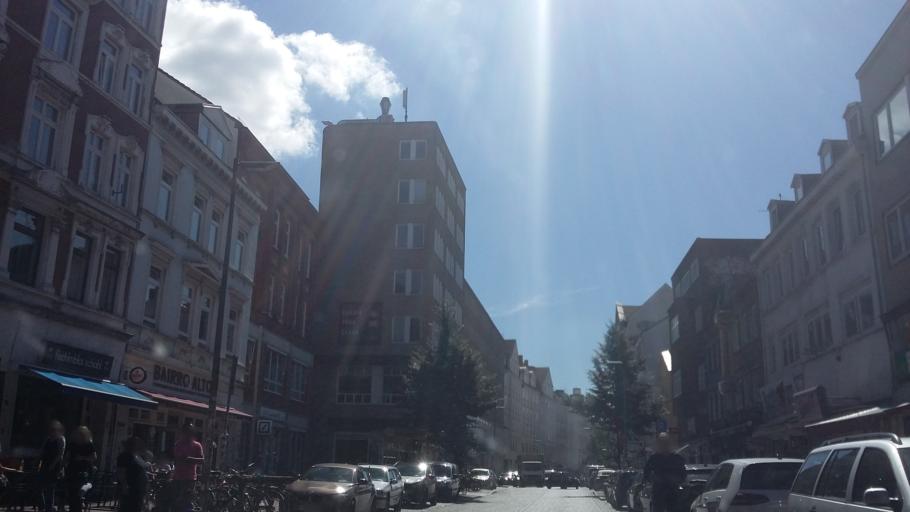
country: DE
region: Hamburg
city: St. Pauli
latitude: 53.5616
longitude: 9.9624
